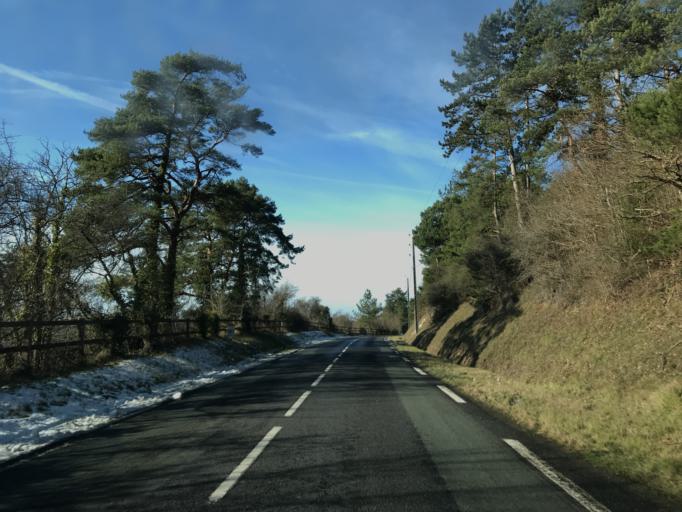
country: FR
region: Haute-Normandie
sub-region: Departement de l'Eure
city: Houlbec-Cocherel
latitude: 49.0637
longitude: 1.3229
